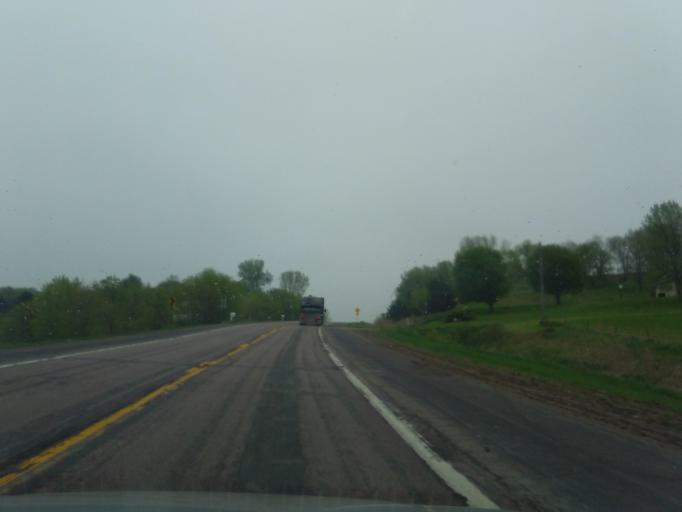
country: US
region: Nebraska
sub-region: Burt County
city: Oakland
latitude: 41.8205
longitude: -96.4700
